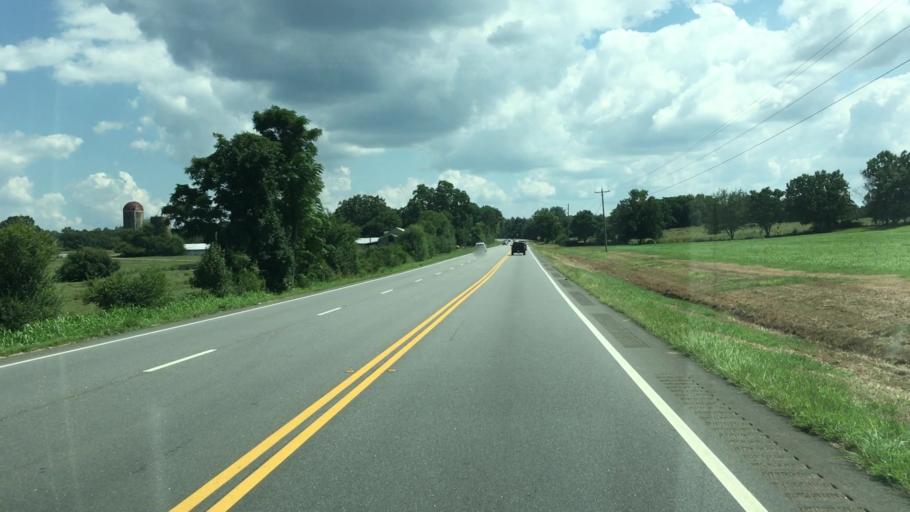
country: US
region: Georgia
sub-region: Morgan County
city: Madison
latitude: 33.4807
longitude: -83.4342
